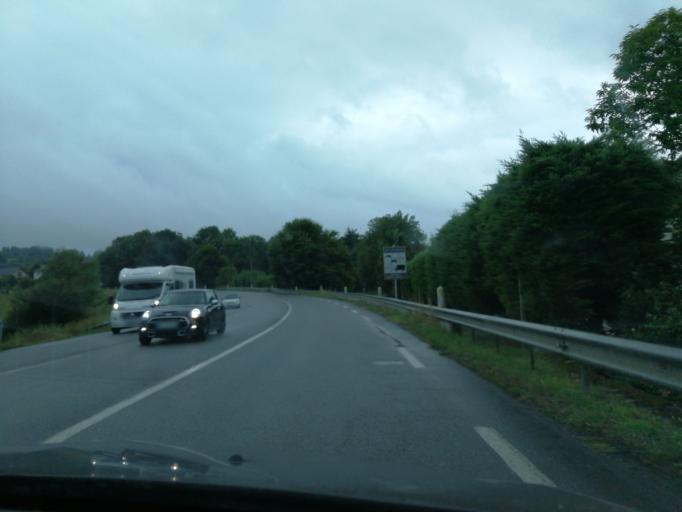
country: FR
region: Aquitaine
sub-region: Departement des Pyrenees-Atlantiques
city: Arudy
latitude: 43.1729
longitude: -0.4404
